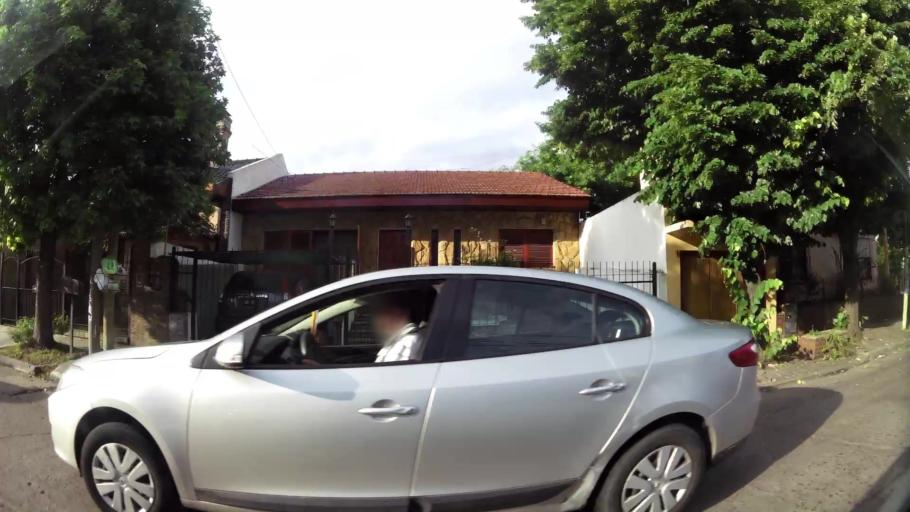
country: AR
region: Buenos Aires
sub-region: Partido de Moron
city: Moron
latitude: -34.6384
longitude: -58.6325
